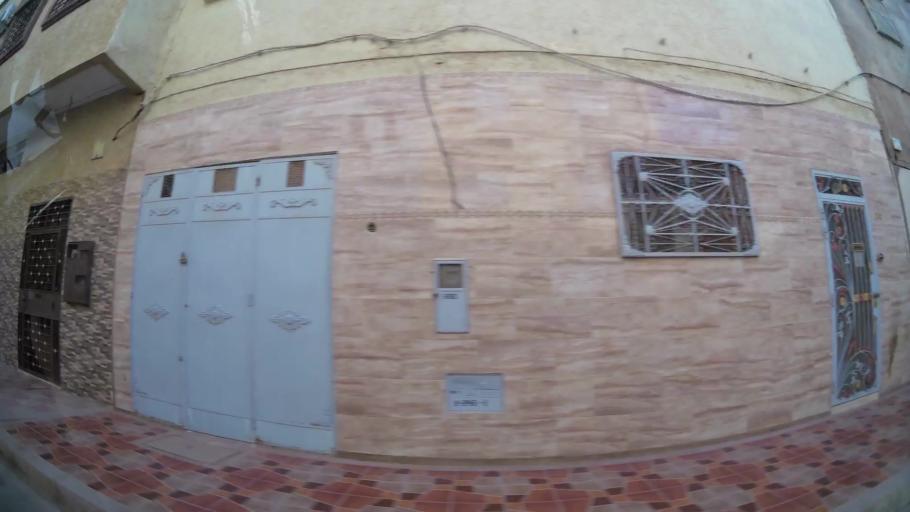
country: MA
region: Oriental
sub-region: Oujda-Angad
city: Oujda
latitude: 34.6885
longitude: -1.9088
